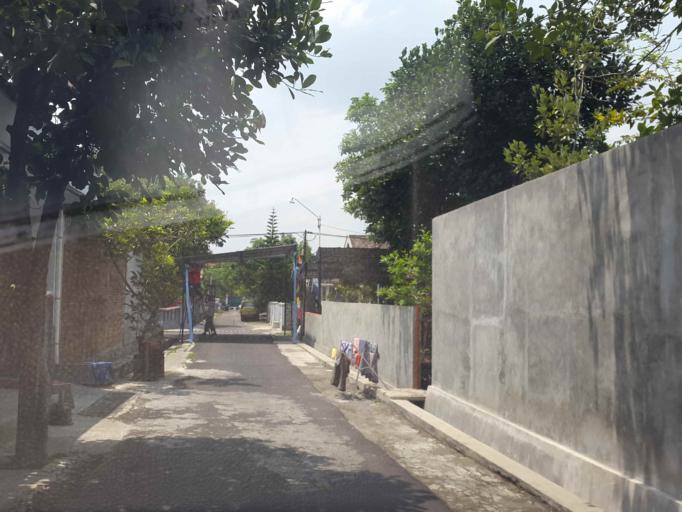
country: ID
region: Central Java
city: Jaten
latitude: -7.5916
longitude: 110.9383
